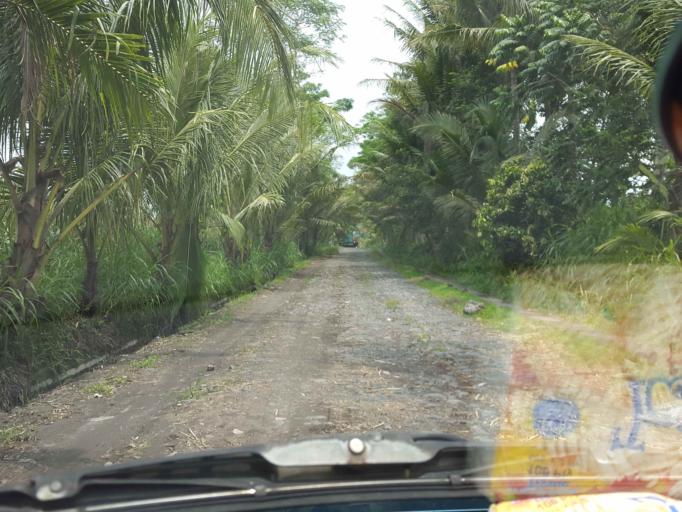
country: ID
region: Central Java
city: Muntilan
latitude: -7.5973
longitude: 110.3163
